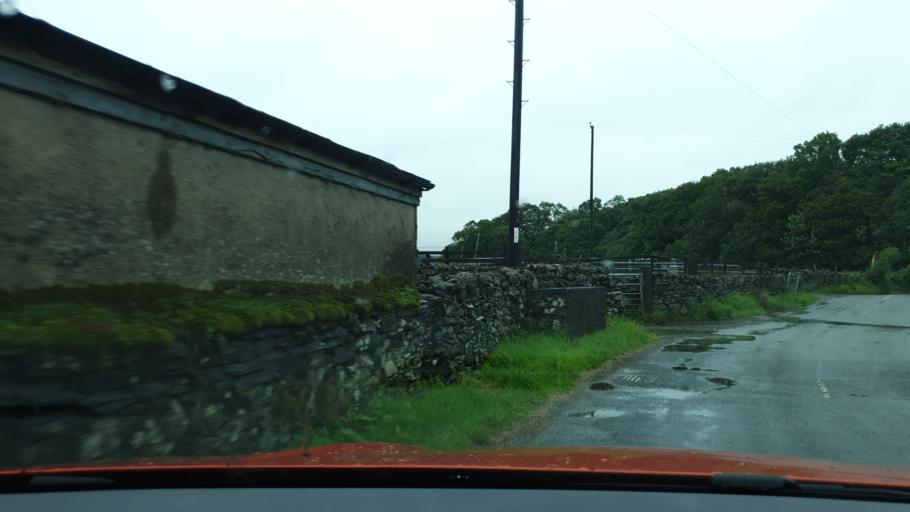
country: GB
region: England
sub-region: Cumbria
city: Ulverston
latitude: 54.2490
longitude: -3.0529
